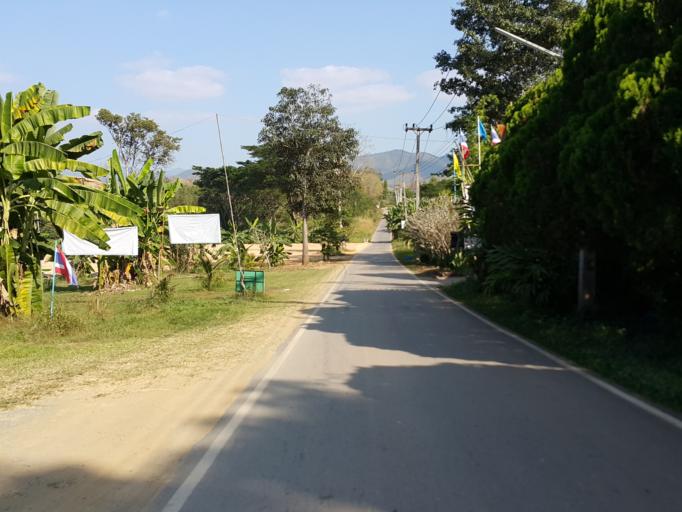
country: TH
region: Chiang Mai
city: Mae On
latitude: 18.7894
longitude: 99.2385
